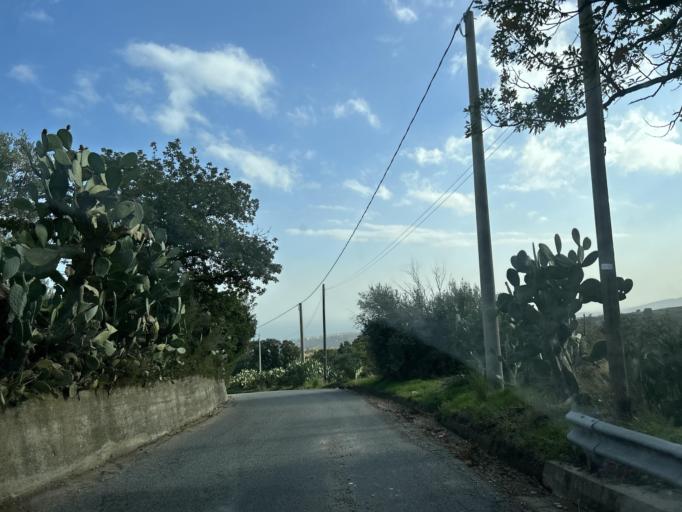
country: IT
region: Calabria
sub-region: Provincia di Catanzaro
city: Montepaone
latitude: 38.7194
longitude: 16.5051
